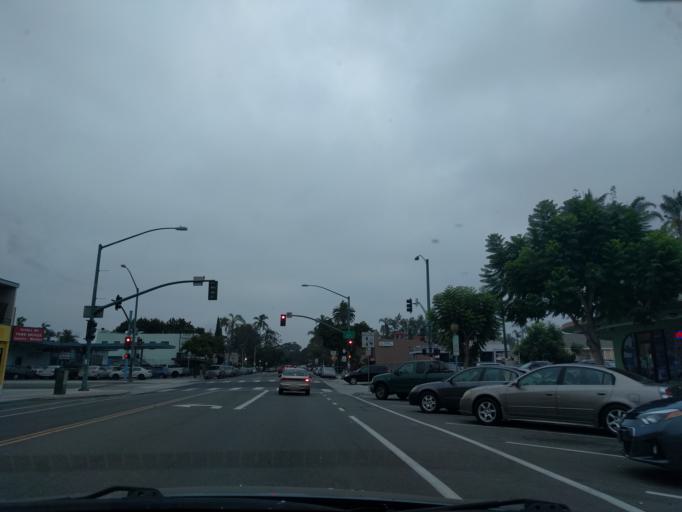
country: US
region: California
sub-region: San Diego County
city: San Diego
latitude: 32.7164
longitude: -117.1403
